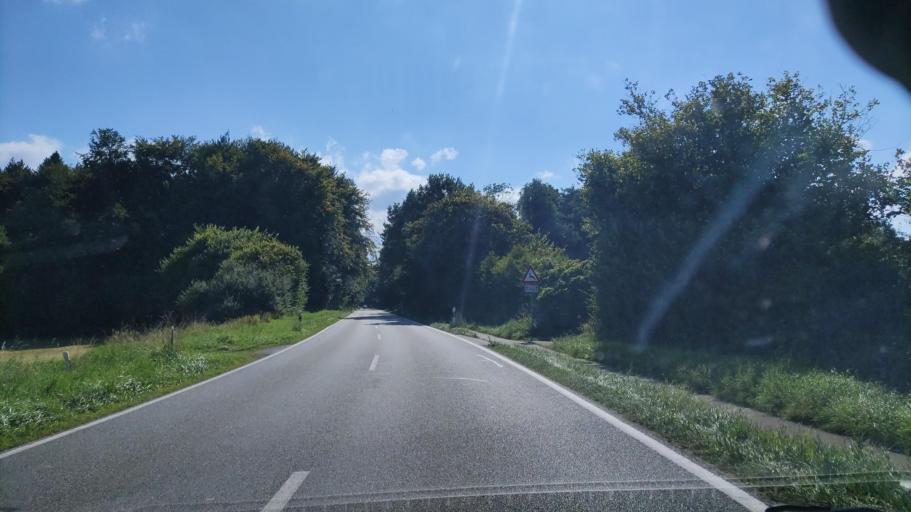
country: DE
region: Schleswig-Holstein
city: Ascheffel
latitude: 54.4287
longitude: 9.7061
